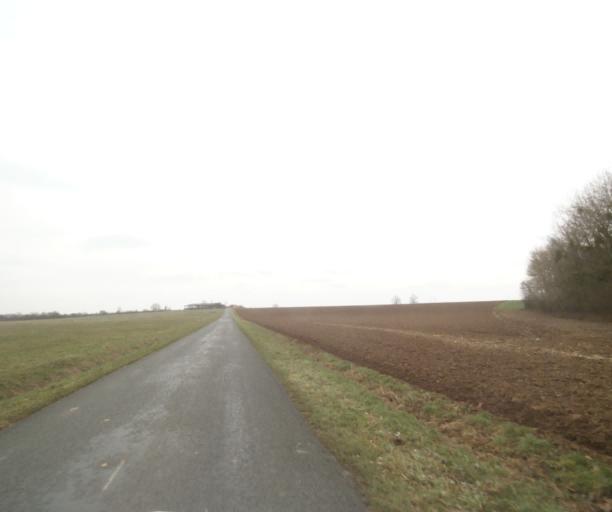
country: FR
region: Champagne-Ardenne
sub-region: Departement de la Marne
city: Pargny-sur-Saulx
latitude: 48.7381
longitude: 4.8260
